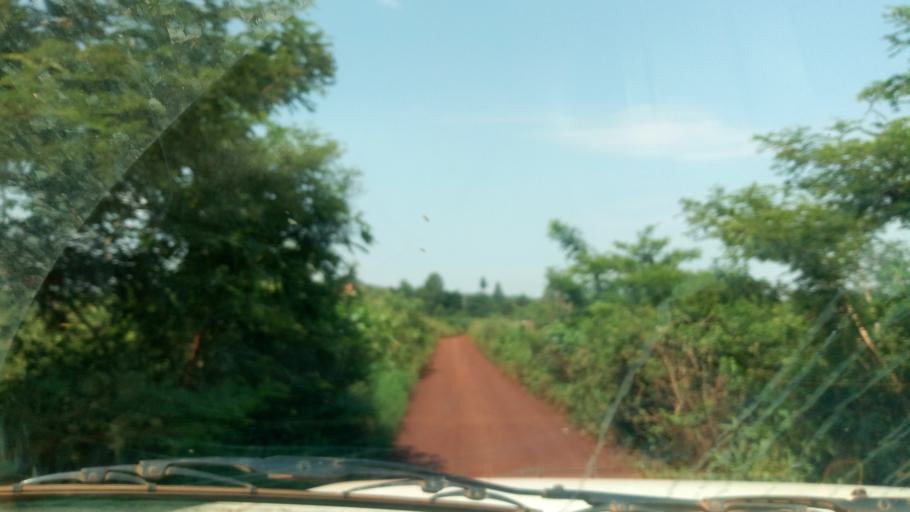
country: UG
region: Western Region
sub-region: Masindi District
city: Masindi
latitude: 1.6716
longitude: 31.8265
